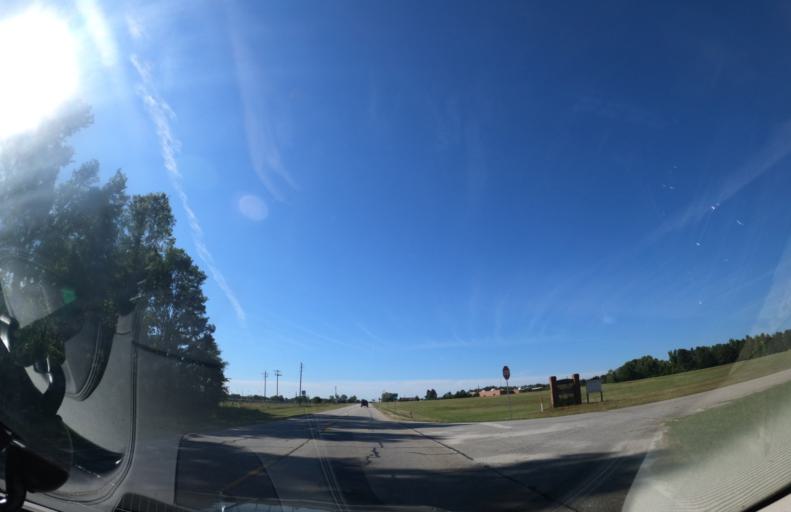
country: US
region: Georgia
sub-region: Jefferson County
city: Wrens
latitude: 33.2235
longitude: -82.3791
